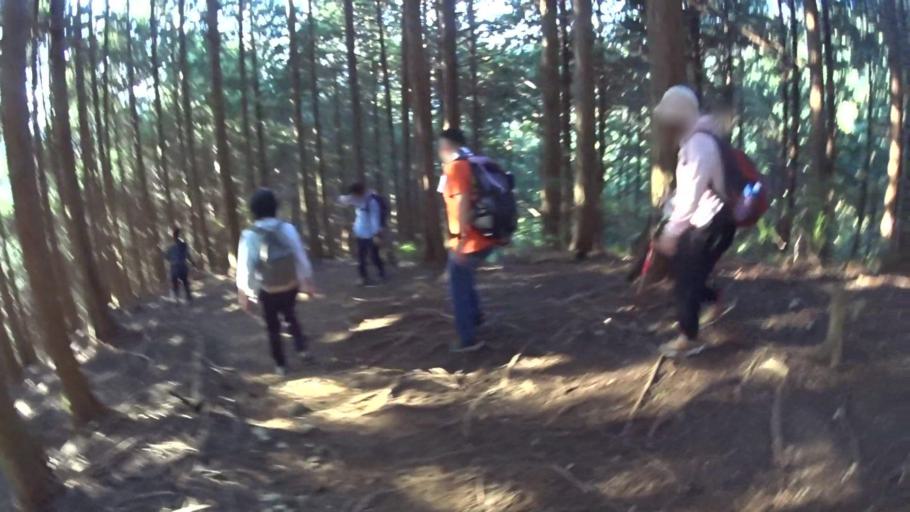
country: JP
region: Shiga Prefecture
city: Kitahama
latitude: 35.1087
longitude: 135.8394
